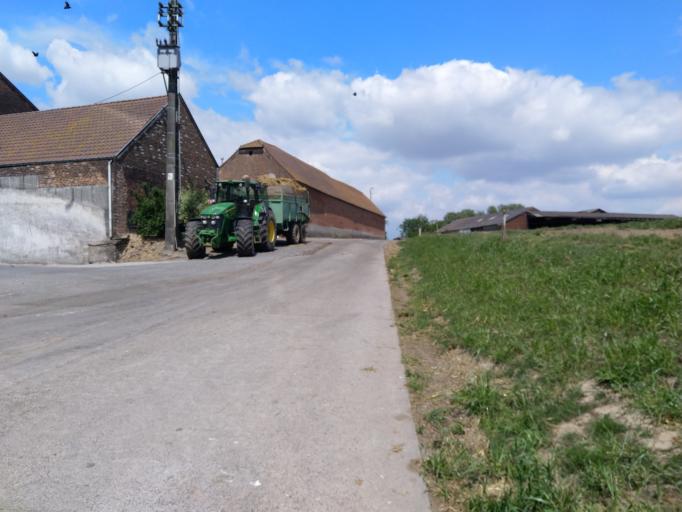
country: BE
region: Wallonia
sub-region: Province du Hainaut
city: Soignies
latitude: 50.6197
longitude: 4.0320
